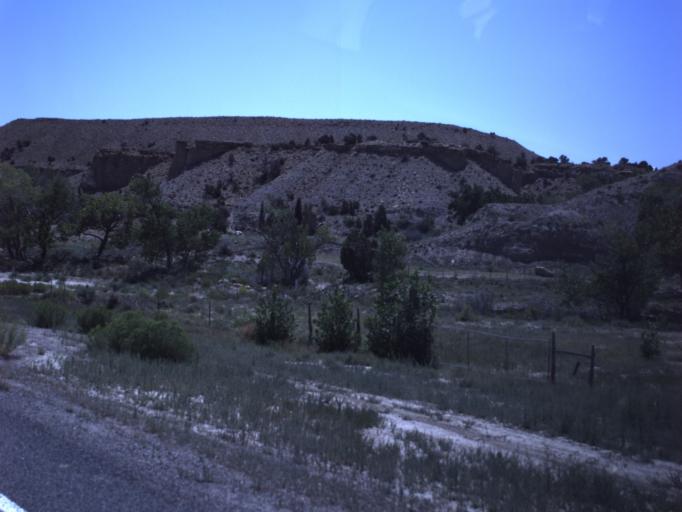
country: US
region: Utah
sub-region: Emery County
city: Orangeville
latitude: 39.2355
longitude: -111.0857
